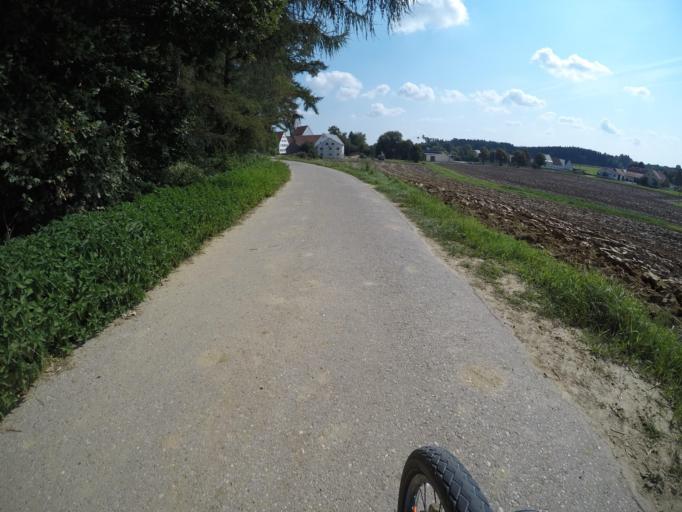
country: DE
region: Bavaria
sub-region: Swabia
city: Laugna
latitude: 48.5547
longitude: 10.7114
